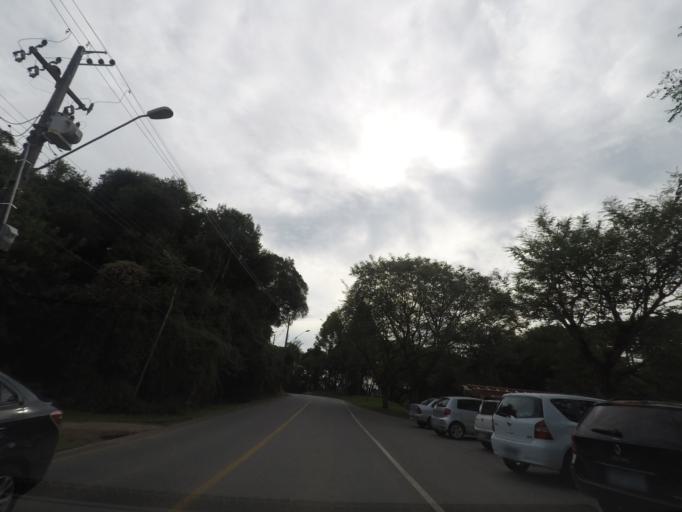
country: BR
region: Parana
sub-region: Curitiba
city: Curitiba
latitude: -25.3954
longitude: -49.3060
